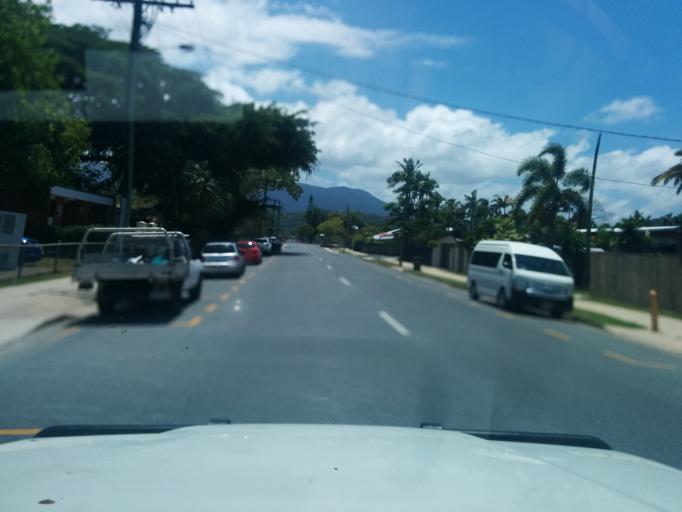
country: AU
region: Queensland
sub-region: Cairns
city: Cairns
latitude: -16.9052
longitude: 145.7436
